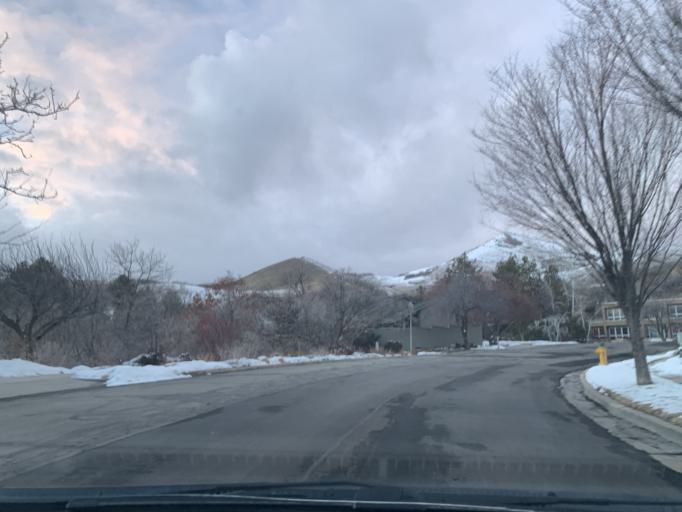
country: US
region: Utah
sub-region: Salt Lake County
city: Salt Lake City
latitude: 40.7819
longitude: -111.8448
